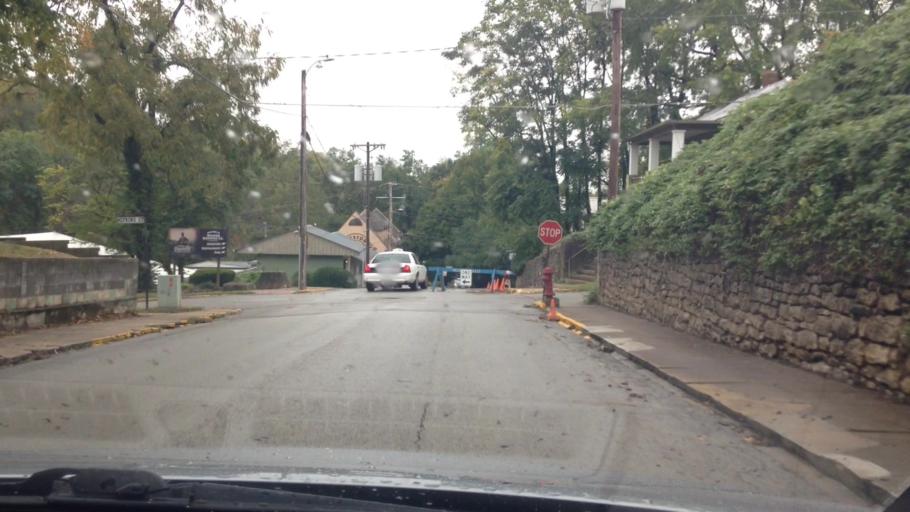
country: US
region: Missouri
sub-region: Platte County
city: Weston
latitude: 39.4121
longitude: -94.8995
